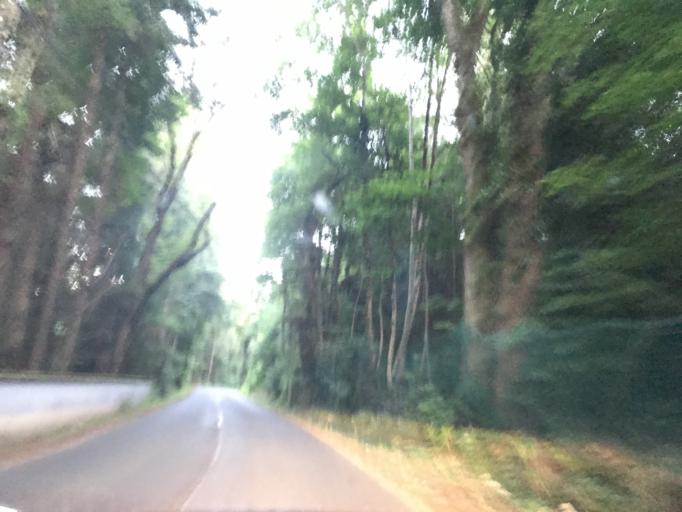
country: FR
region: Auvergne
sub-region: Departement du Puy-de-Dome
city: Thiers
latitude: 45.8757
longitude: 3.5591
